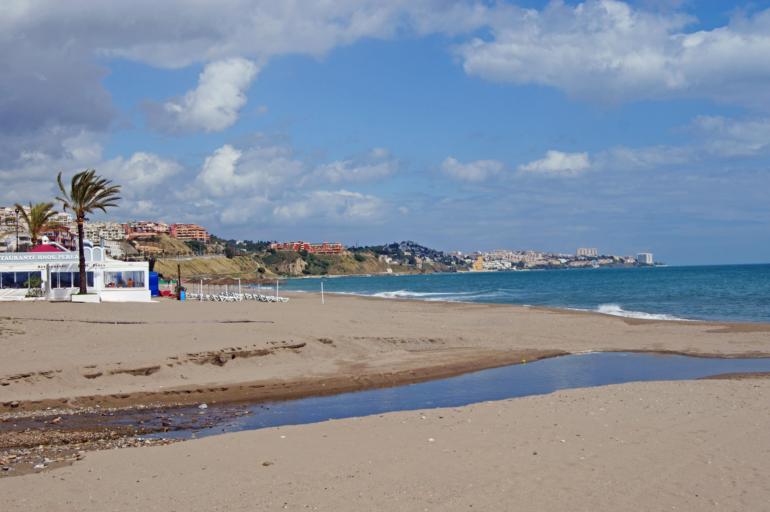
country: ES
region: Andalusia
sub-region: Provincia de Malaga
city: Benalmadena
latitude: 36.5673
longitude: -4.5958
